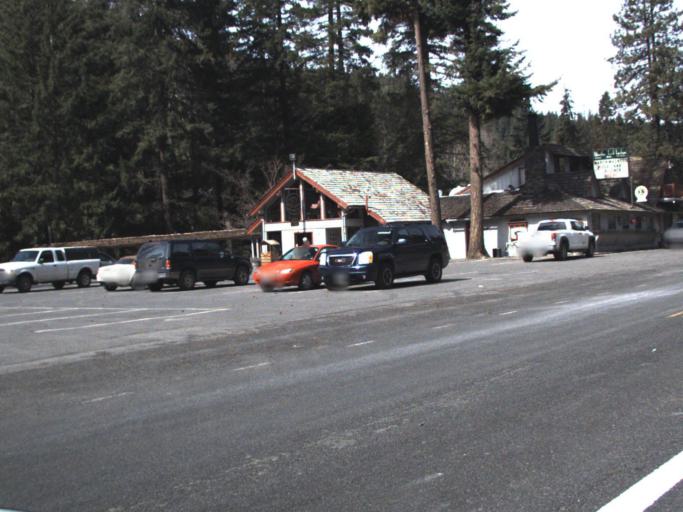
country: US
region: Washington
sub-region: Kittitas County
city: Cle Elum
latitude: 46.9411
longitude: -121.0630
